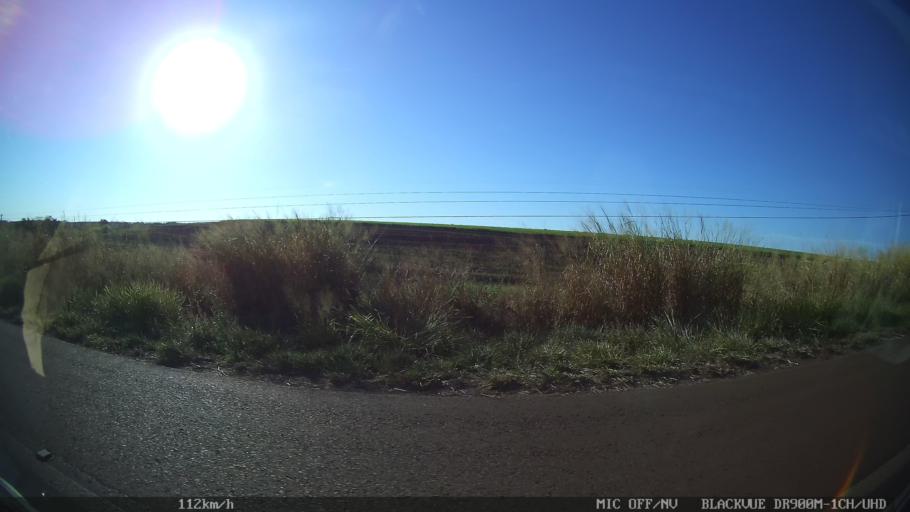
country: BR
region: Sao Paulo
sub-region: Guapiacu
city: Guapiacu
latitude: -20.7393
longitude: -49.0904
